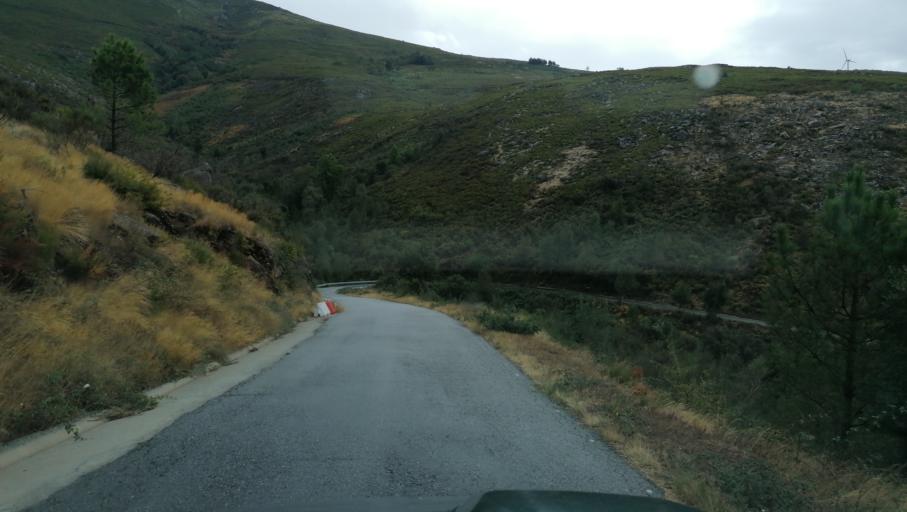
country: PT
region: Vila Real
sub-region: Vila Pouca de Aguiar
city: Vila Pouca de Aguiar
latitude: 41.5570
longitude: -7.7011
